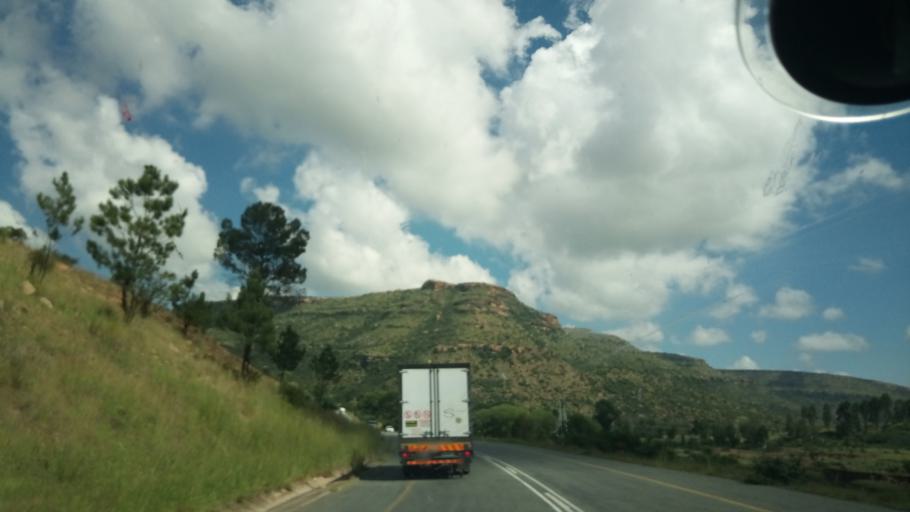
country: ZA
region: Orange Free State
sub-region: Thabo Mofutsanyana District Municipality
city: Ficksburg
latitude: -28.8892
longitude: 27.8399
